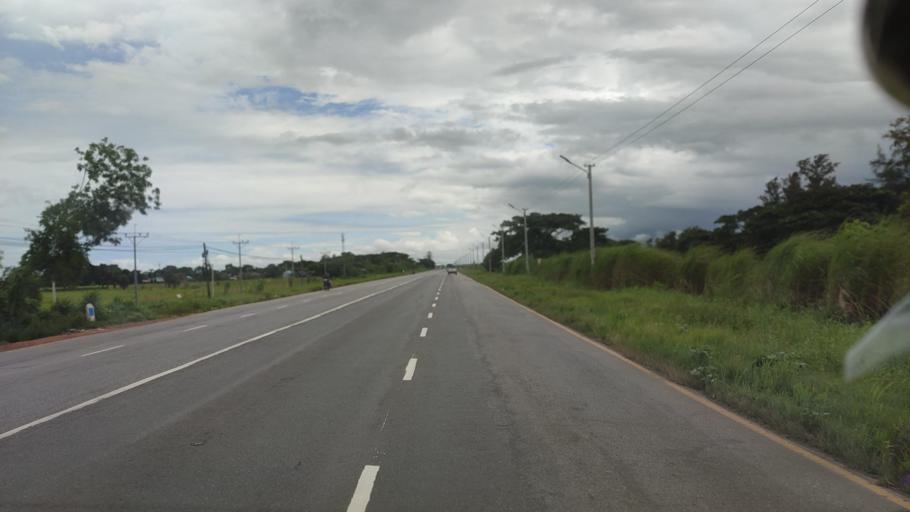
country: MM
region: Bago
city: Bago
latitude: 17.4209
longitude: 96.5228
